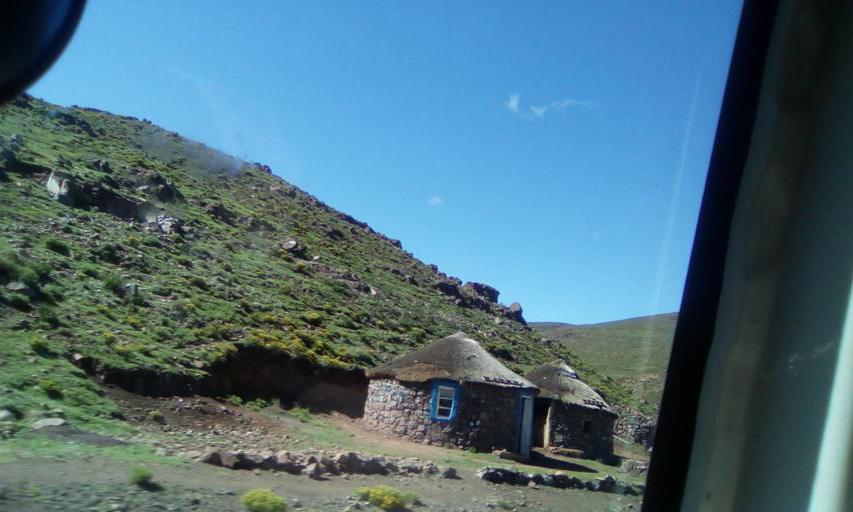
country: LS
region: Maseru
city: Nako
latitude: -29.8913
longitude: 28.1180
